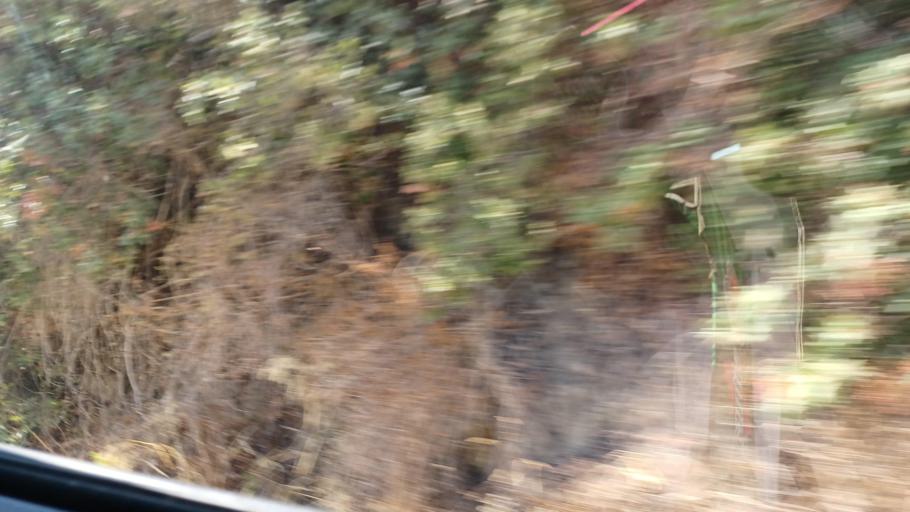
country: CY
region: Pafos
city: Polis
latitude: 34.9612
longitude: 32.4686
